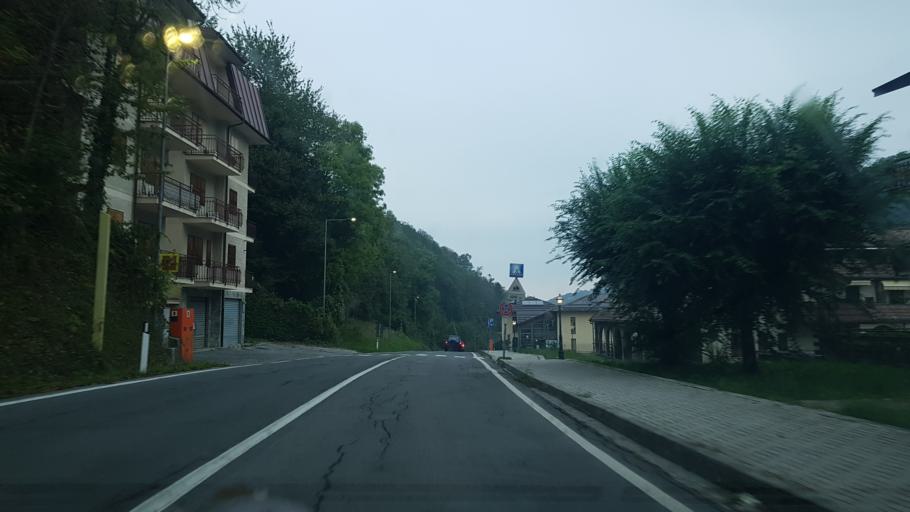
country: IT
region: Piedmont
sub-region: Provincia di Cuneo
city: Frabosa Sottana
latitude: 44.3046
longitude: 7.8005
